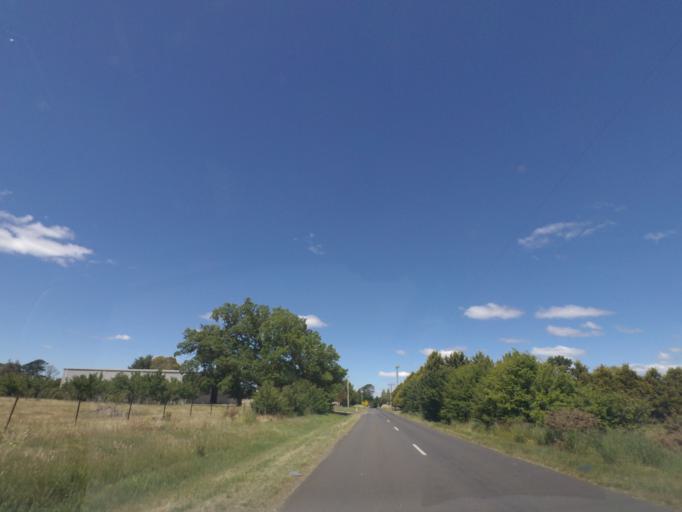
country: AU
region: Victoria
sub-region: Mount Alexander
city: Castlemaine
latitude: -37.2376
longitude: 144.4128
